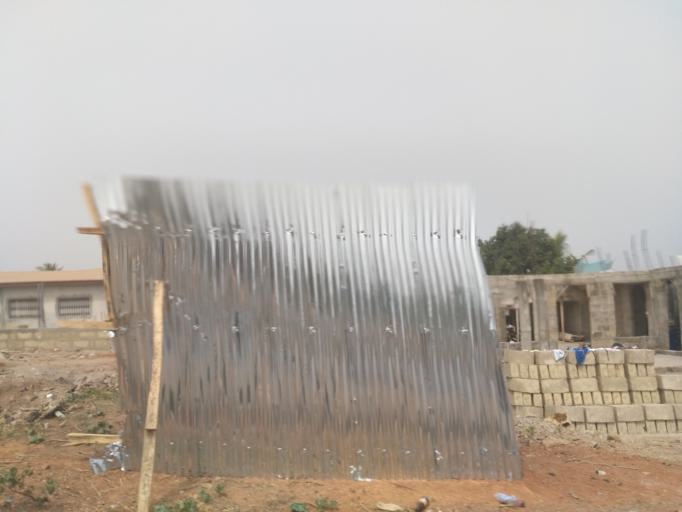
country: GH
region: Ashanti
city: Mamponteng
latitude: 6.6655
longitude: -1.5456
